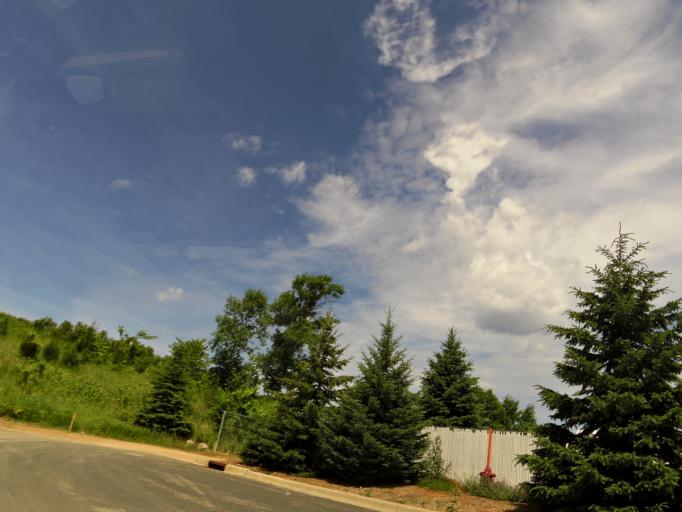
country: US
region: Minnesota
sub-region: Scott County
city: Shakopee
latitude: 44.7452
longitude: -93.4892
